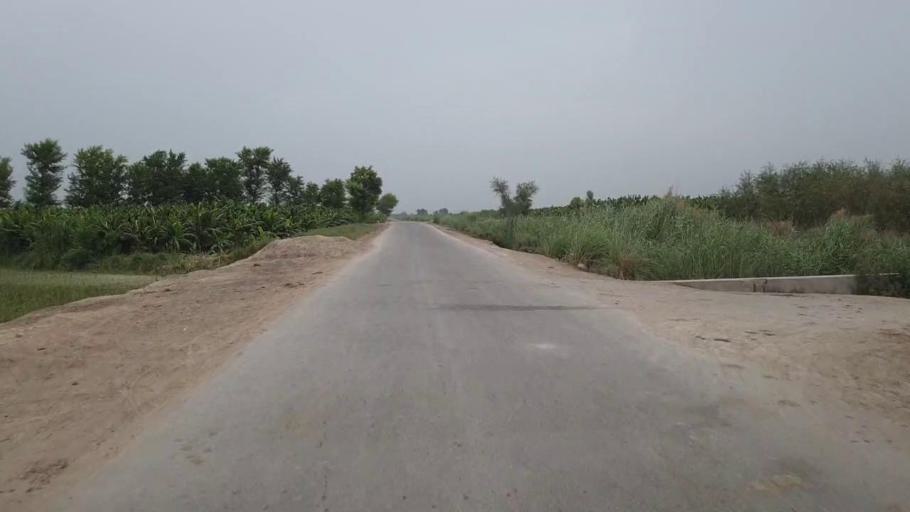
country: PK
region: Sindh
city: Bandhi
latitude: 26.5553
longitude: 68.2092
